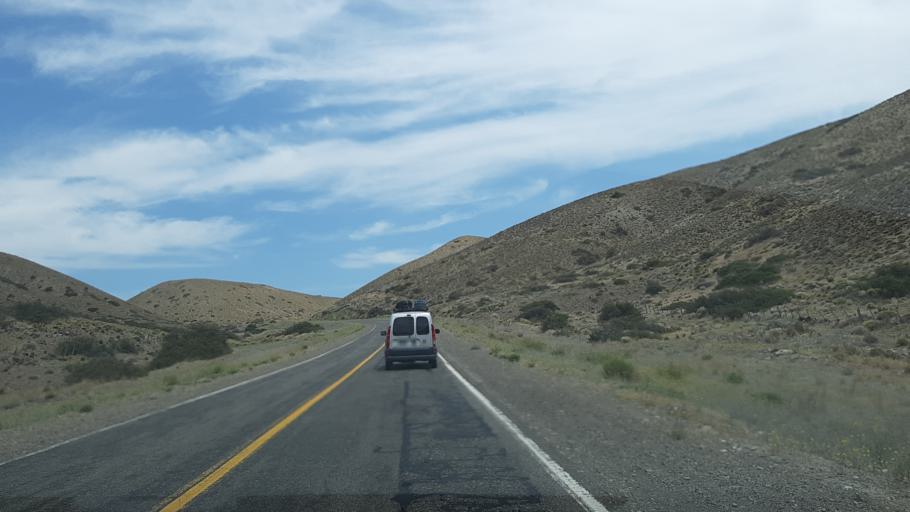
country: AR
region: Rio Negro
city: Pilcaniyeu
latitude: -40.4745
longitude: -70.6616
